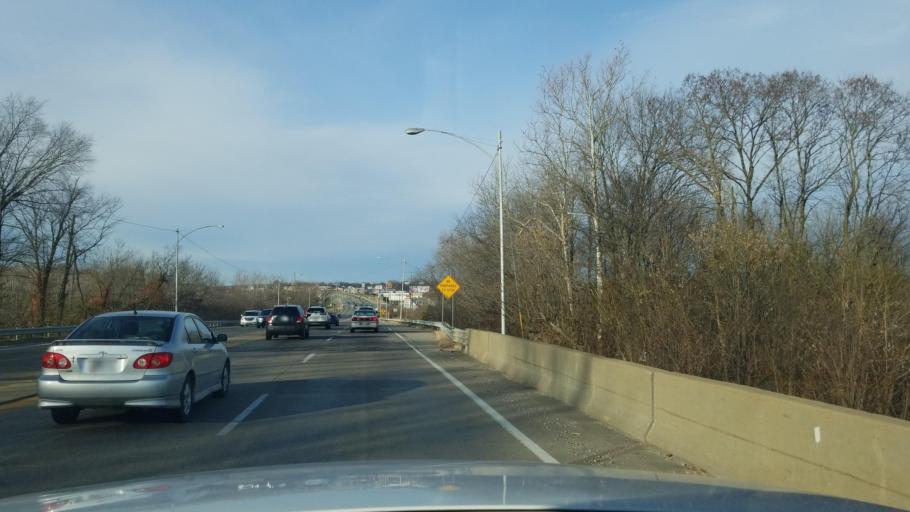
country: US
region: Indiana
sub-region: Vanderburgh County
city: Evansville
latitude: 37.9777
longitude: -87.6211
